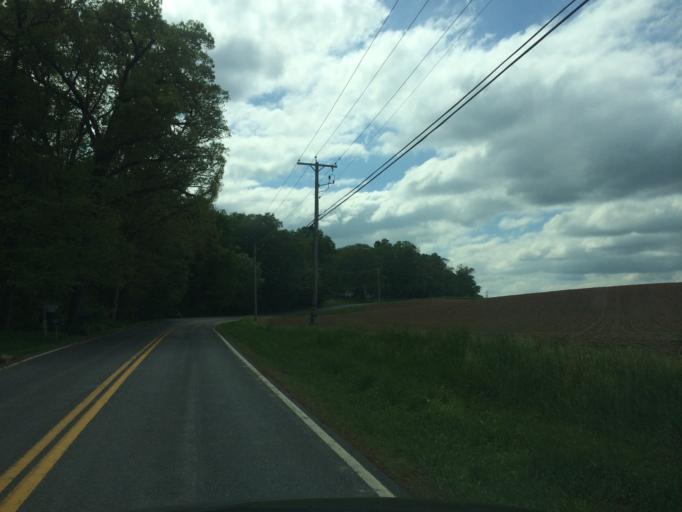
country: US
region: Maryland
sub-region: Carroll County
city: Sykesville
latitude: 39.3238
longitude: -76.9700
